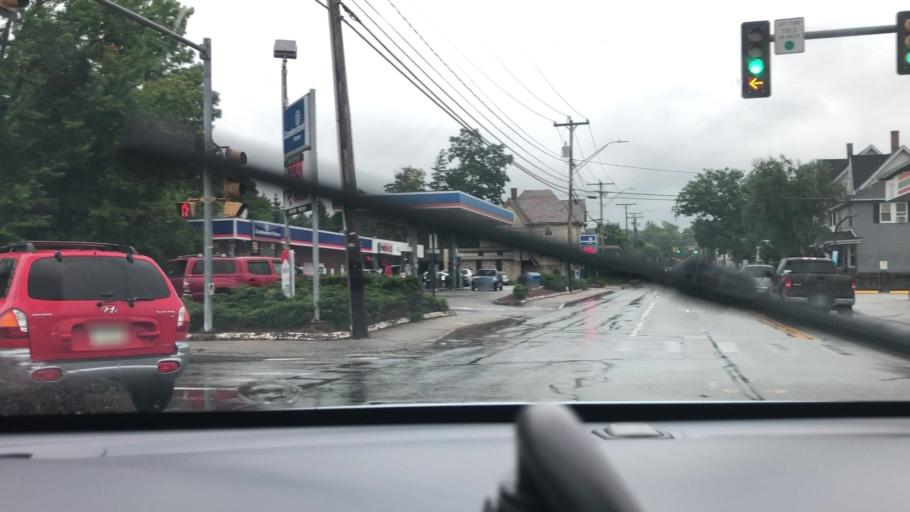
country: US
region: New Hampshire
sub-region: Hillsborough County
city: Manchester
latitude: 43.0069
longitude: -71.4600
